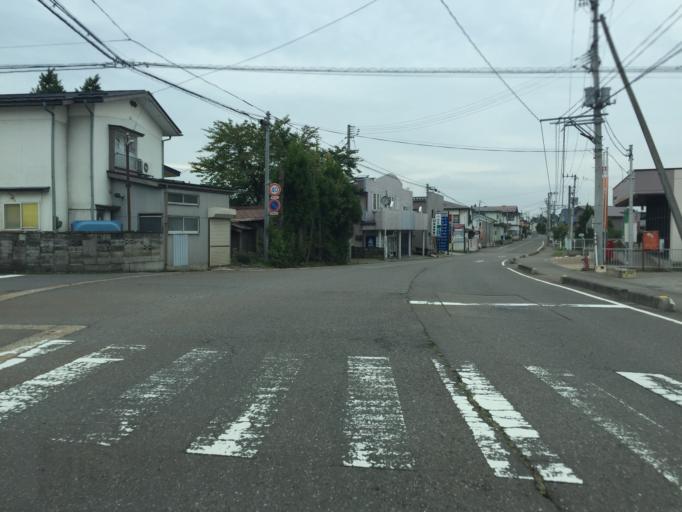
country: JP
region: Fukushima
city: Kitakata
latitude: 37.5483
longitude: 139.9286
